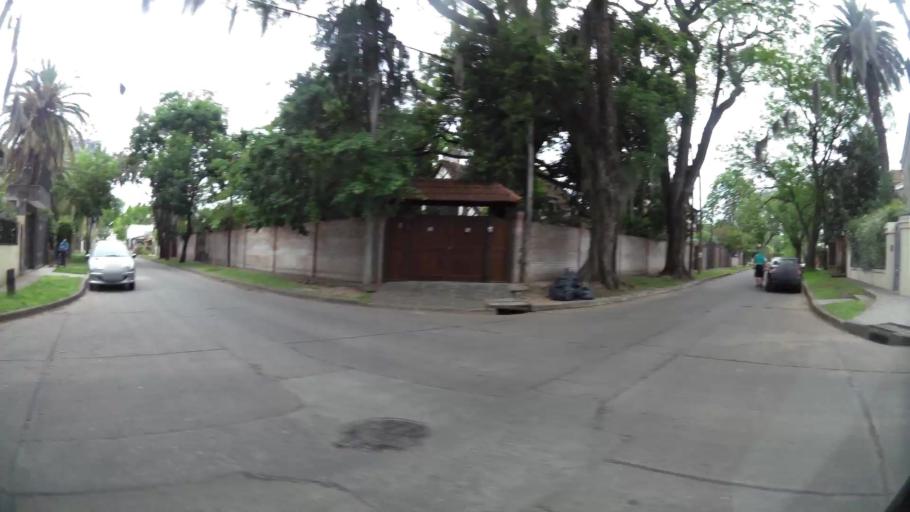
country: AR
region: Santa Fe
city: Granadero Baigorria
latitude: -32.8799
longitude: -60.6895
